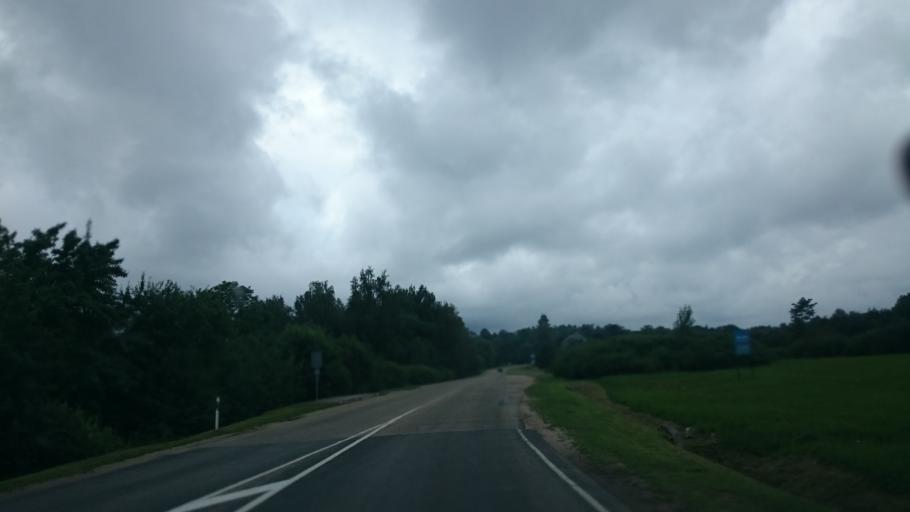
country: LV
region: Pavilostas
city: Pavilosta
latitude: 56.8791
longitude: 21.2236
